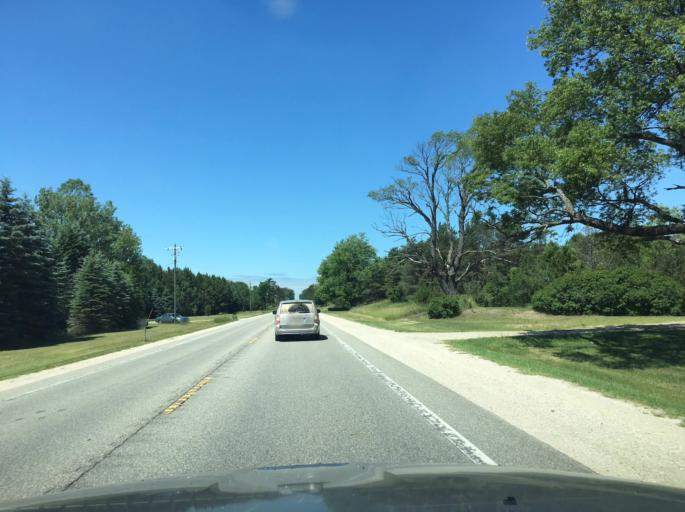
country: US
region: Michigan
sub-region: Osceola County
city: Reed City
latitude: 43.8876
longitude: -85.5440
